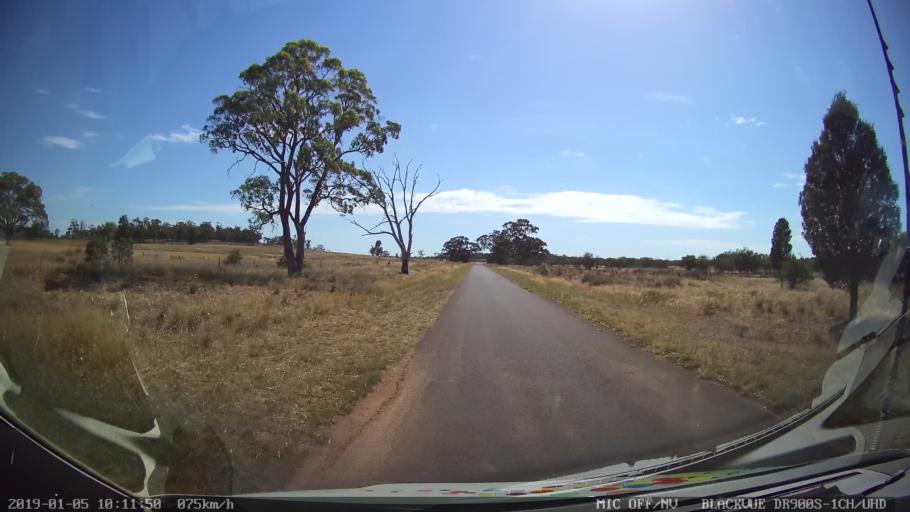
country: AU
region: New South Wales
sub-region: Gilgandra
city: Gilgandra
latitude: -31.6111
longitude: 148.9059
